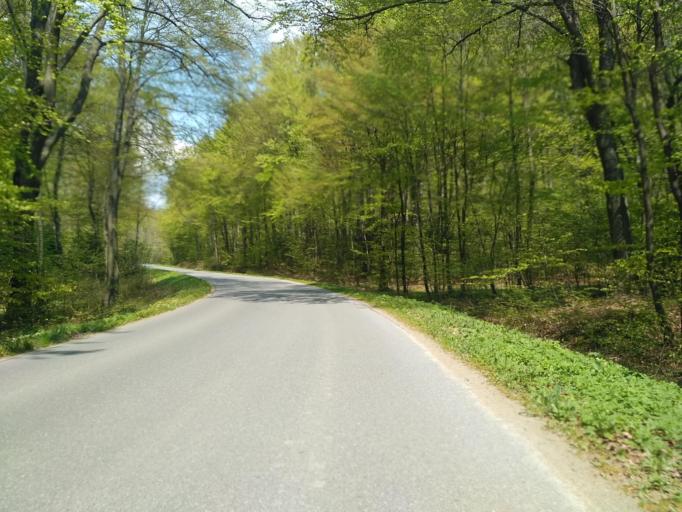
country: PL
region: Subcarpathian Voivodeship
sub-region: Powiat jasielski
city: Debowiec
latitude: 49.7047
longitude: 21.5120
